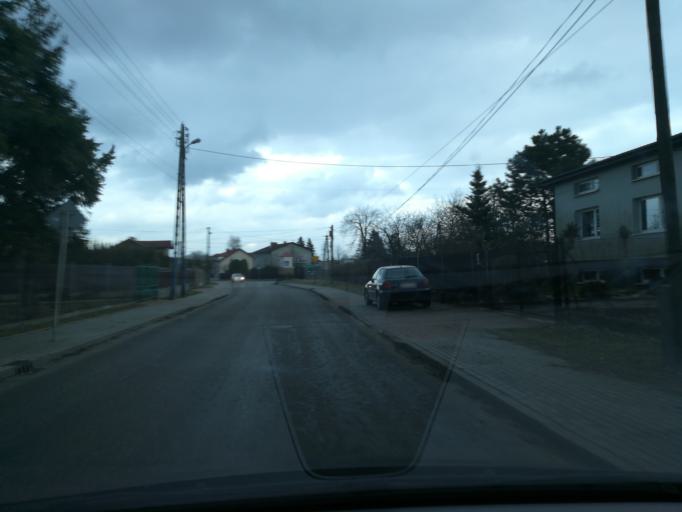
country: PL
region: Lodz Voivodeship
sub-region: Powiat radomszczanski
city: Radomsko
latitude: 51.0603
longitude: 19.4223
